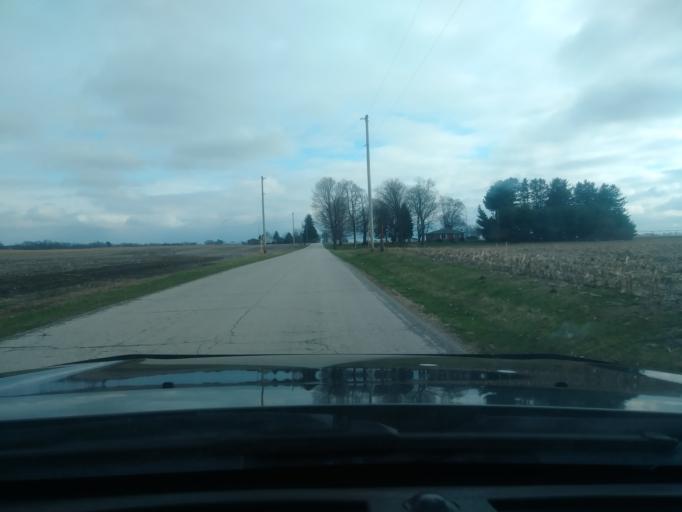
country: US
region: Indiana
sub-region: LaPorte County
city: LaPorte
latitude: 41.5839
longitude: -86.7980
